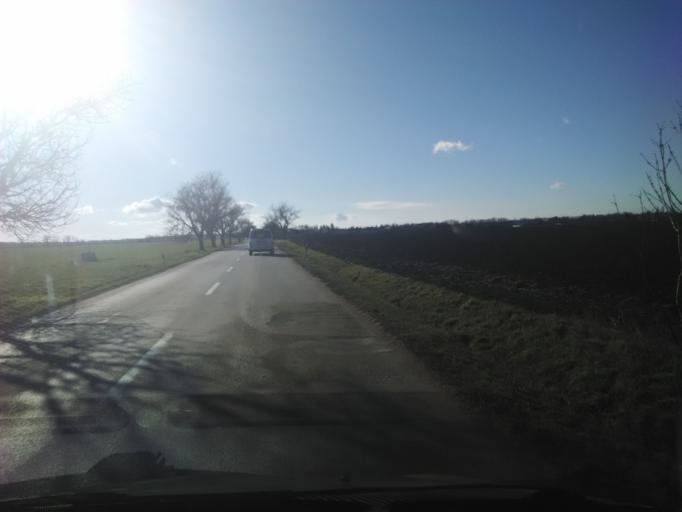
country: SK
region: Nitriansky
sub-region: Okres Nitra
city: Vrable
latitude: 48.2016
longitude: 18.2093
